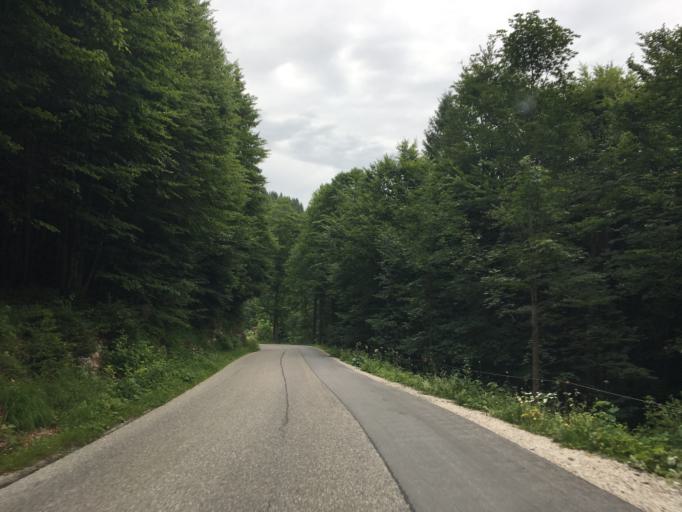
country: AT
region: Salzburg
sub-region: Politischer Bezirk Salzburg-Umgebung
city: Strobl
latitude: 47.6598
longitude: 13.4430
